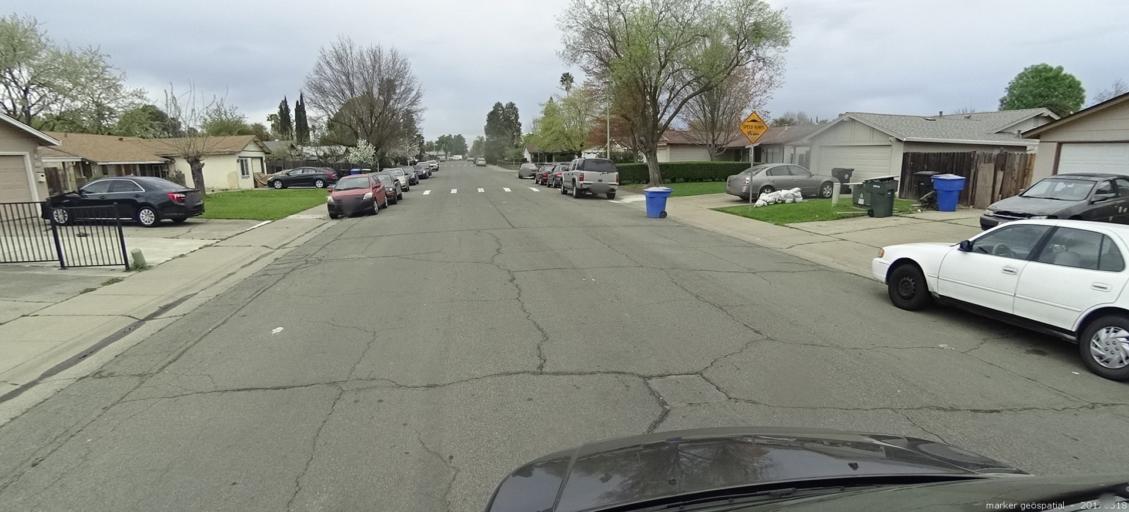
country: US
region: California
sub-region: Sacramento County
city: Parkway
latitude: 38.4762
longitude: -121.4355
